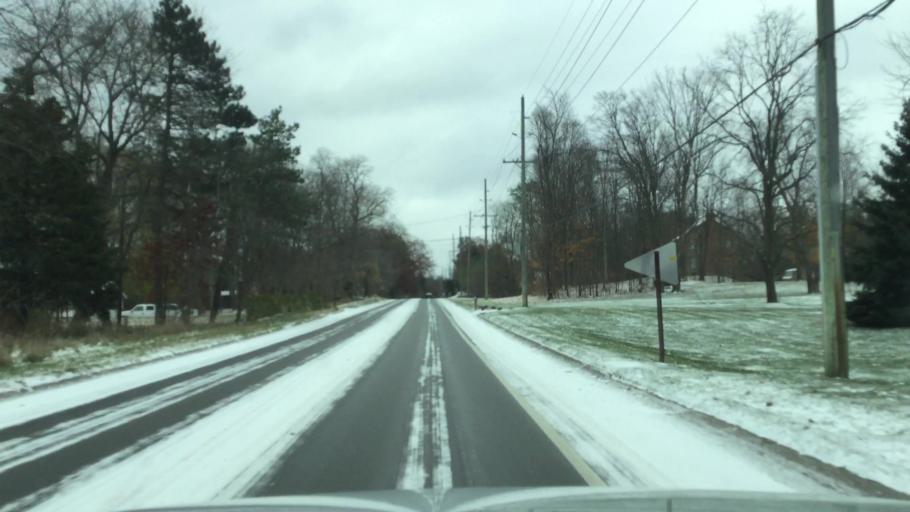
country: US
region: Michigan
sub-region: Livingston County
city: Brighton
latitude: 42.5281
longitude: -83.8347
